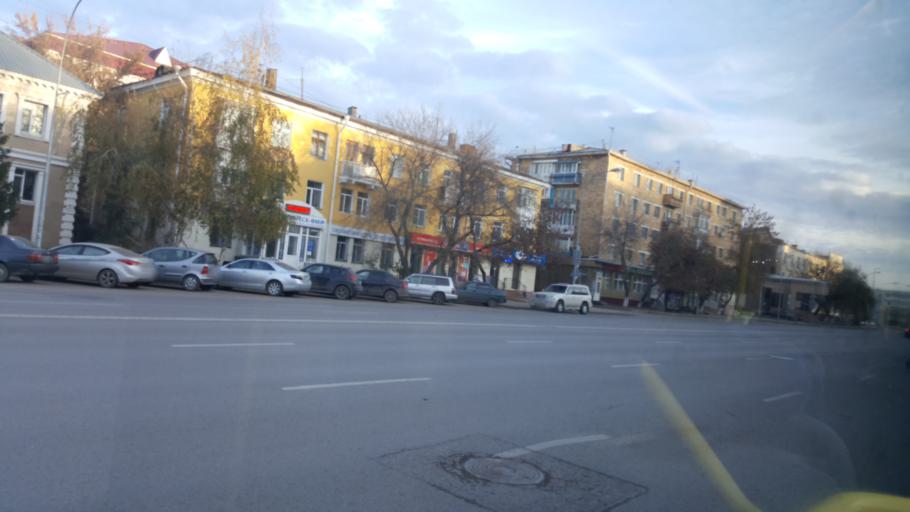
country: KZ
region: Astana Qalasy
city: Astana
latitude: 51.1687
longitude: 71.4131
